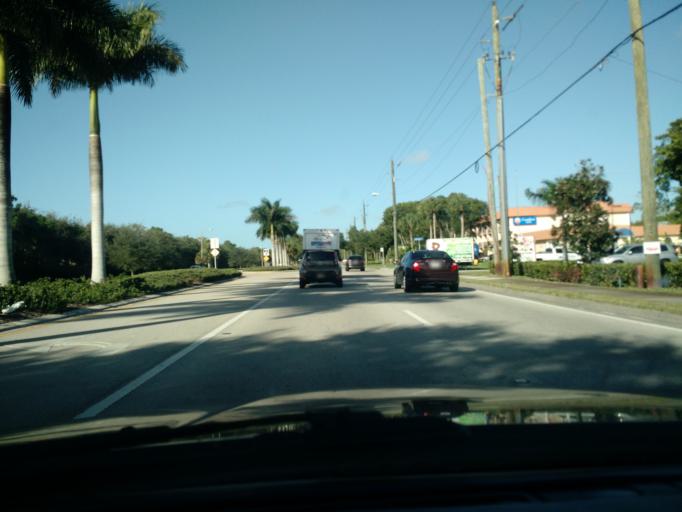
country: US
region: Florida
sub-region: Lee County
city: Bonita Springs
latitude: 26.3311
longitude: -81.7873
